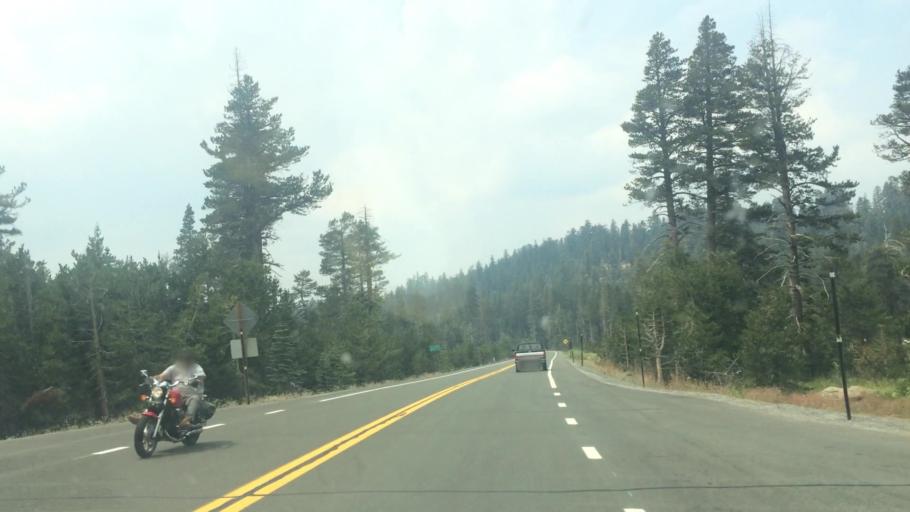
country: US
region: California
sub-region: El Dorado County
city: South Lake Tahoe
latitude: 38.6375
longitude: -120.1421
